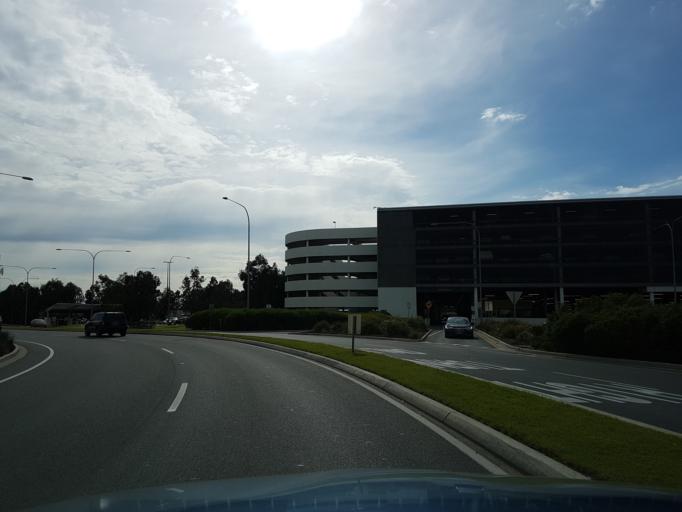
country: AU
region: South Australia
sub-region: City of West Torrens
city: Plympton
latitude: -34.9384
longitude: 138.5348
